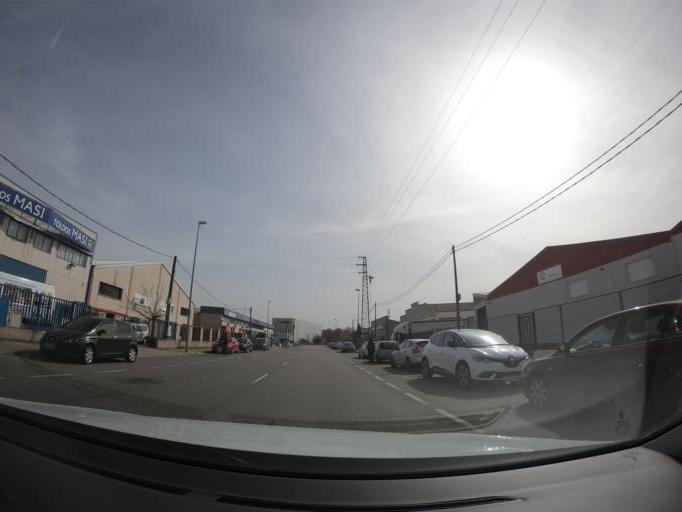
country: ES
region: Basque Country
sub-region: Provincia de Alava
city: Oyon
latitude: 42.4756
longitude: -2.4034
